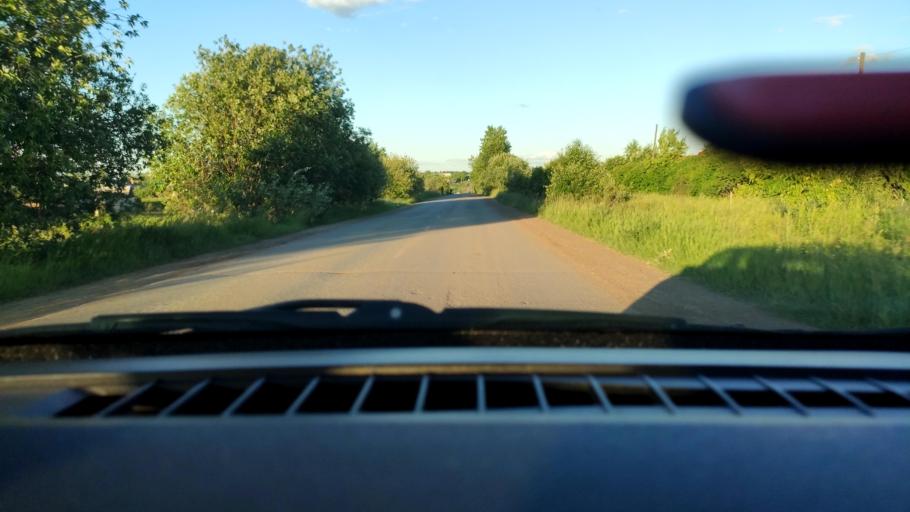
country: RU
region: Perm
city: Kultayevo
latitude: 57.9286
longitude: 55.8688
